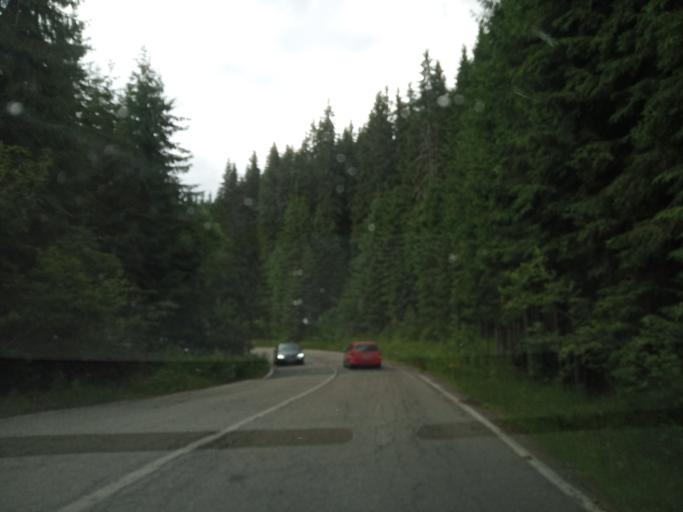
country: RO
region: Valcea
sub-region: Comuna Voineasa
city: Voineasa
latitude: 45.4175
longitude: 23.7339
